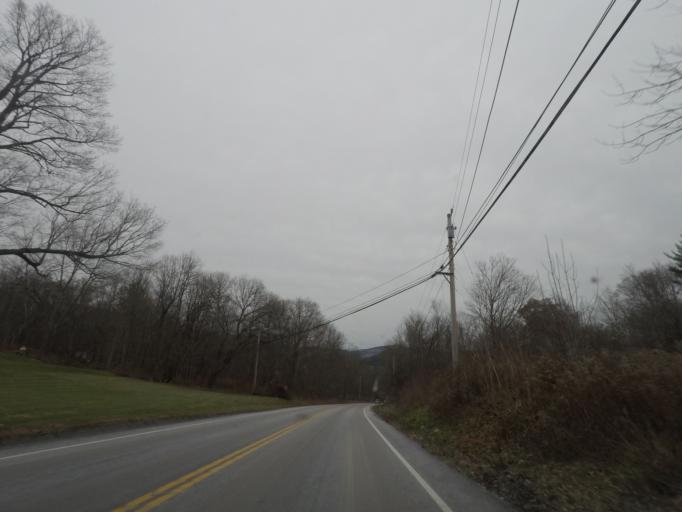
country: US
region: New York
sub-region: Rensselaer County
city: Hoosick Falls
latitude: 42.7543
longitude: -73.3547
